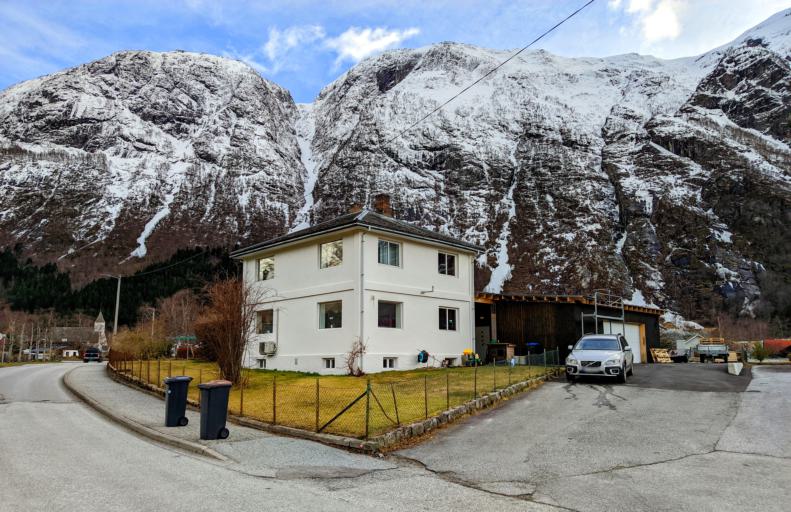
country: NO
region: Hordaland
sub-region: Eidfjord
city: Eidfjord
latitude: 60.4646
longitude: 7.0700
